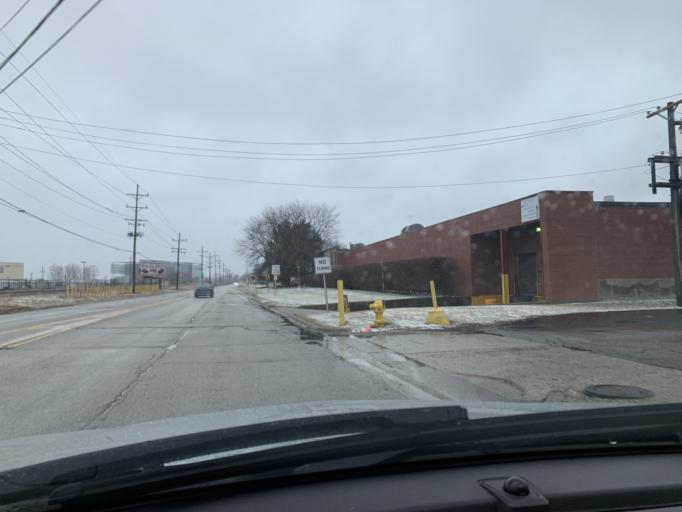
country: US
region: Illinois
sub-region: Cook County
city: Morton Grove
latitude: 42.0181
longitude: -87.7766
